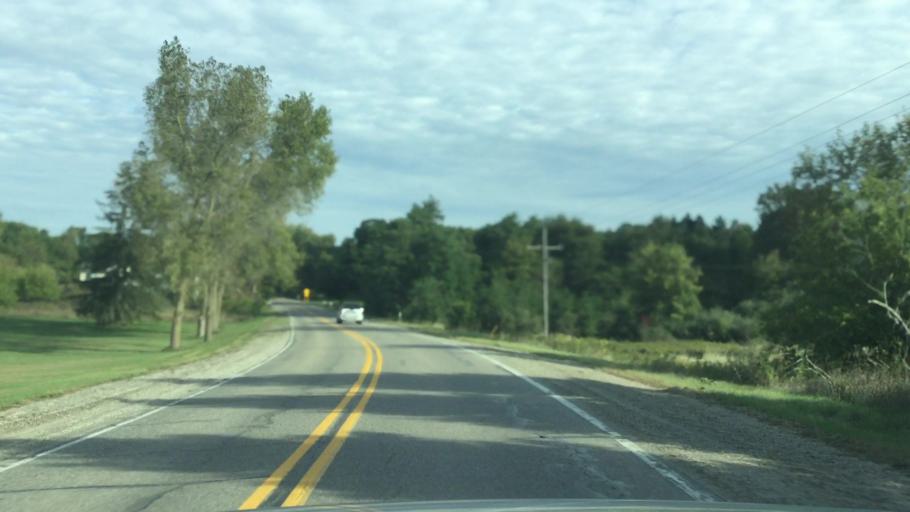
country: US
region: Michigan
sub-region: Livingston County
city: Howell
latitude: 42.5726
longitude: -83.8931
